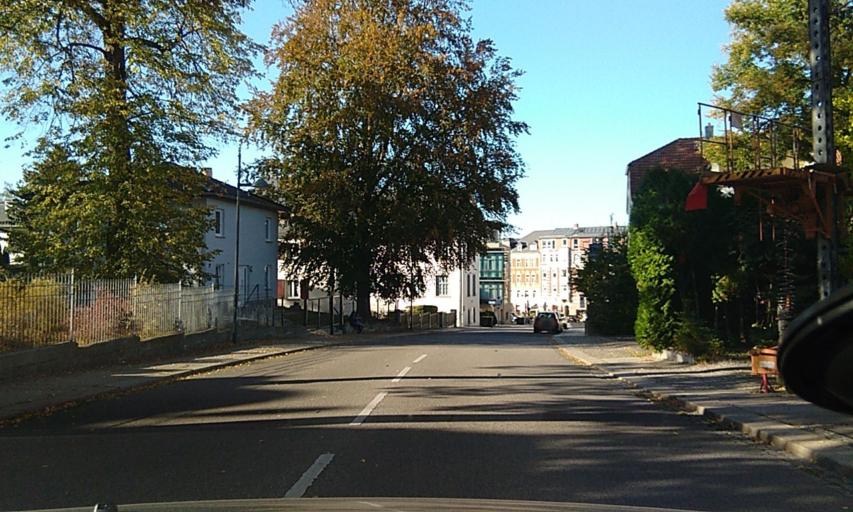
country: DE
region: Saxony
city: Limbach-Oberfrohna
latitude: 50.8575
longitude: 12.7627
